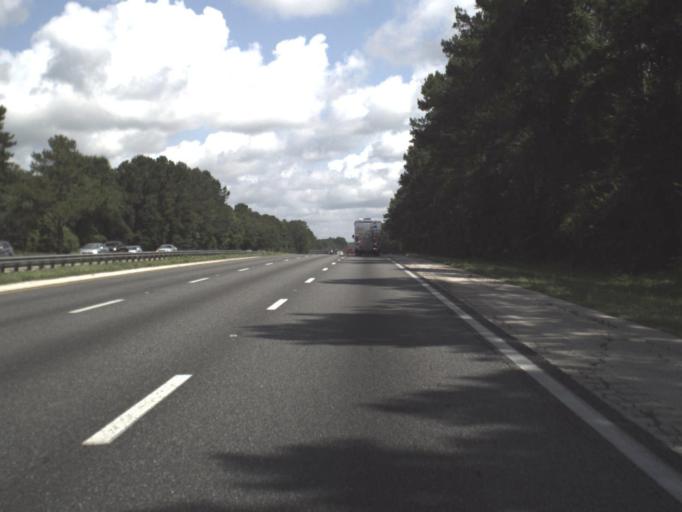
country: US
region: Florida
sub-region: Alachua County
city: High Springs
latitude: 29.8328
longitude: -82.5245
